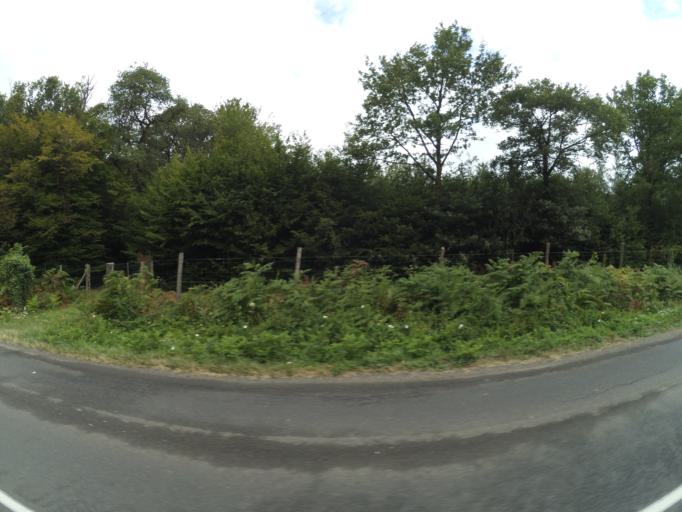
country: FR
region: Pays de la Loire
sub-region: Departement de Maine-et-Loire
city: Villedieu-la-Blouere
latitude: 47.1284
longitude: -1.0872
